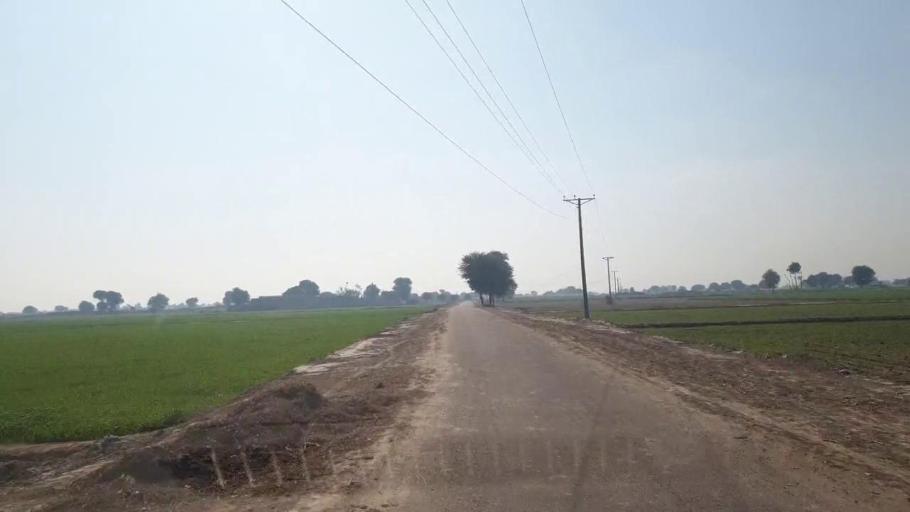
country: PK
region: Sindh
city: Shahpur Chakar
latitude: 26.1046
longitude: 68.6006
